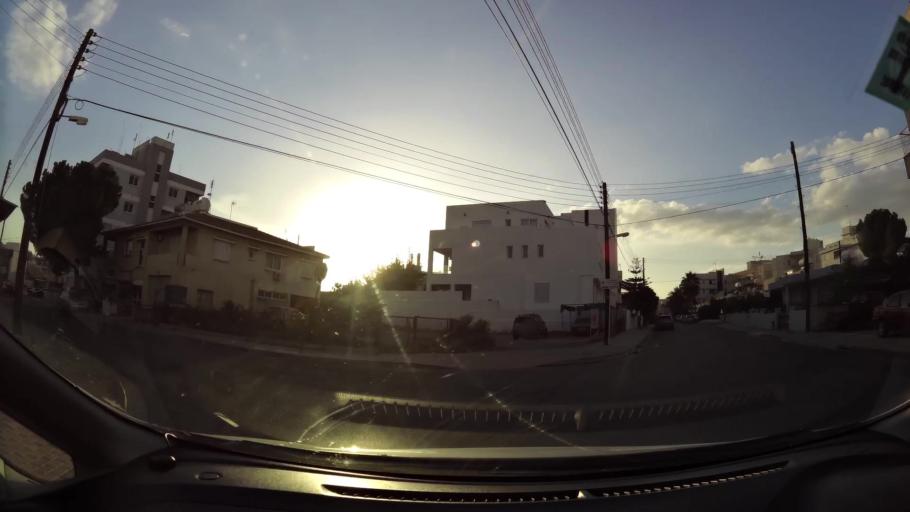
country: CY
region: Lefkosia
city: Nicosia
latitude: 35.1583
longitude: 33.3937
